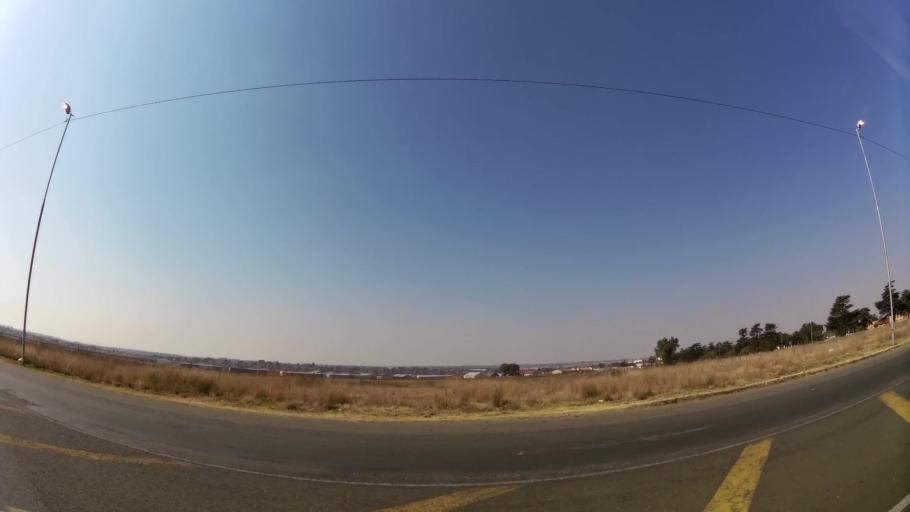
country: ZA
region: Gauteng
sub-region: Ekurhuleni Metropolitan Municipality
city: Boksburg
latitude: -26.2404
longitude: 28.2942
